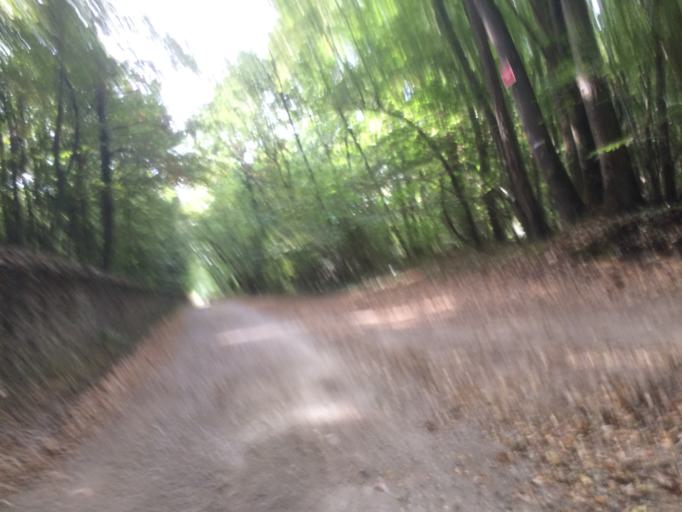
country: FR
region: Ile-de-France
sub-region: Departement des Yvelines
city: Bonnelles
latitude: 48.6158
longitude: 2.0152
